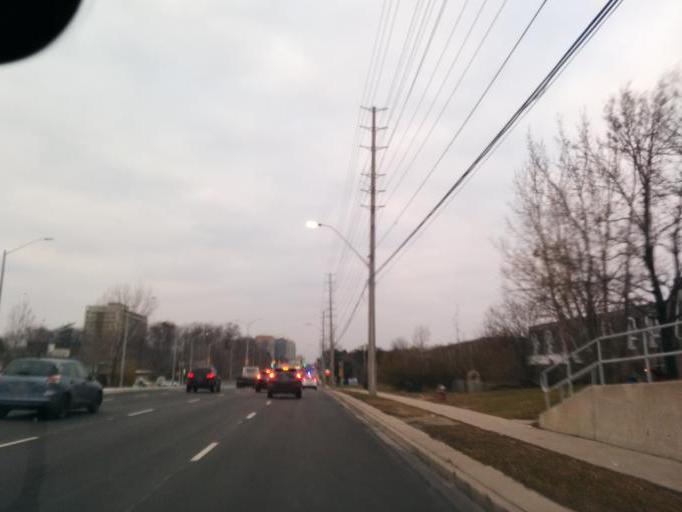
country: CA
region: Ontario
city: Etobicoke
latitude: 43.6186
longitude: -79.5969
